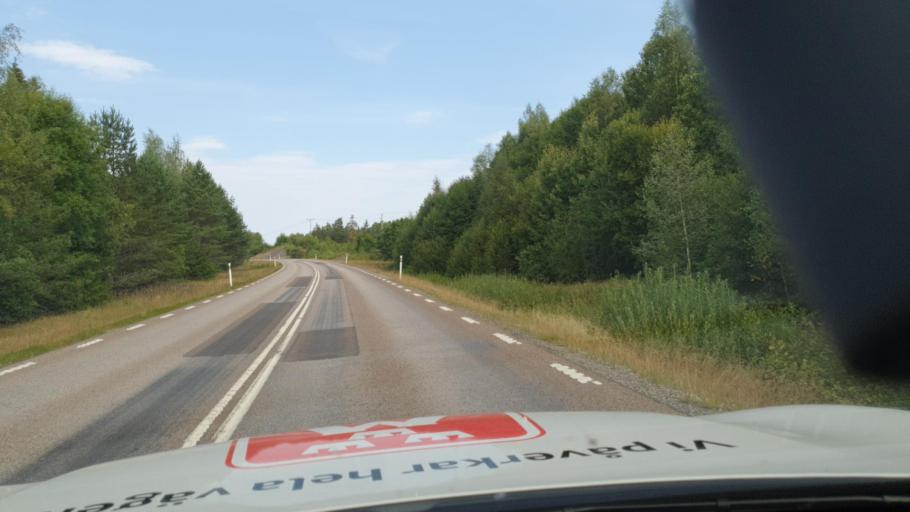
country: SE
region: Vaestra Goetaland
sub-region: Melleruds Kommun
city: Mellerud
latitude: 58.7372
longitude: 12.3542
